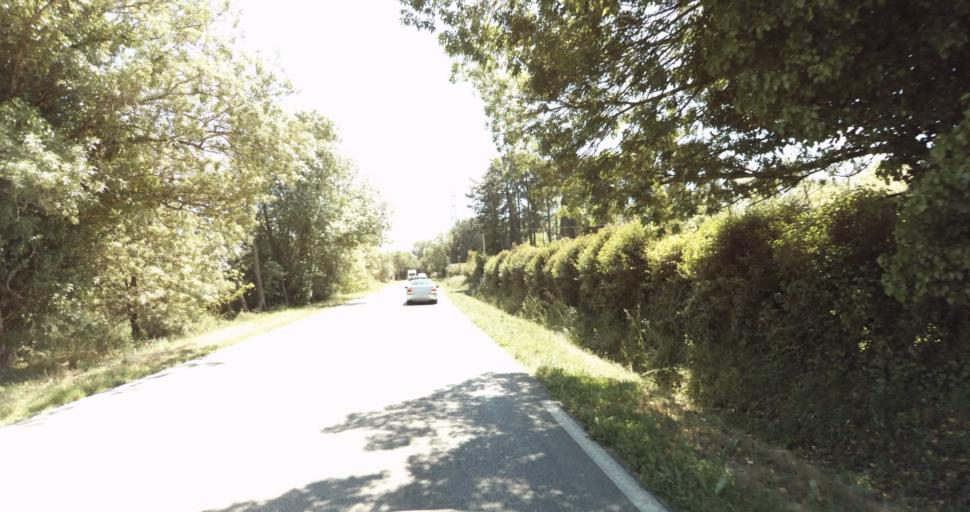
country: FR
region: Provence-Alpes-Cote d'Azur
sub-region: Departement du Var
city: Hyeres
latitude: 43.1376
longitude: 6.1569
